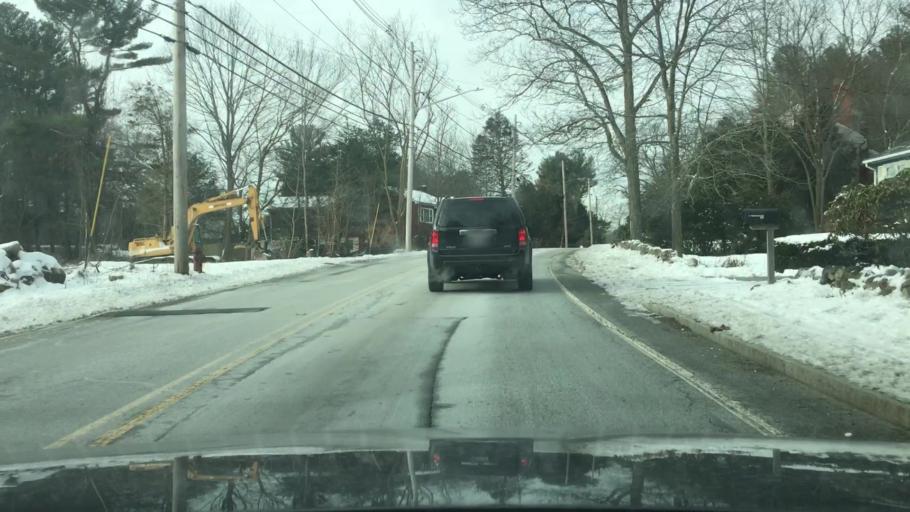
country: US
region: Massachusetts
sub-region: Essex County
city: Middleton
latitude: 42.5754
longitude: -71.0400
